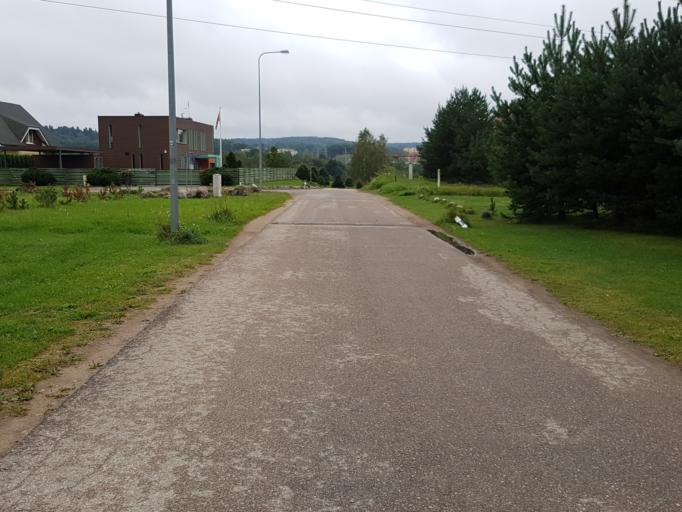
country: LT
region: Vilnius County
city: Lazdynai
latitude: 54.6522
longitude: 25.2081
